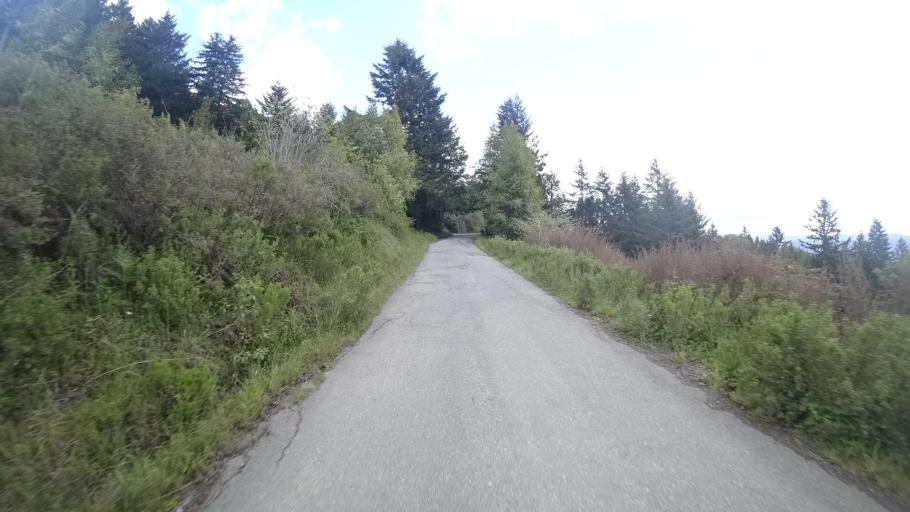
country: US
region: California
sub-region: Humboldt County
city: Blue Lake
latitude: 40.8582
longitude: -123.9290
